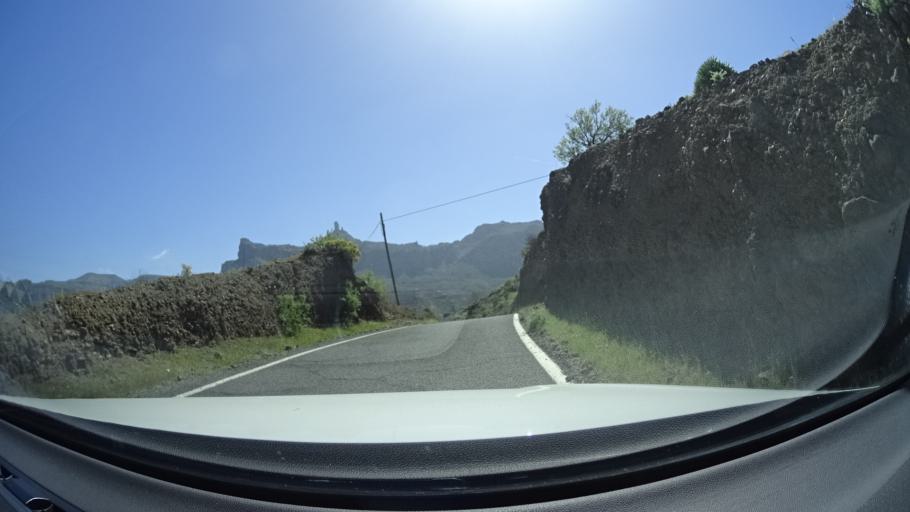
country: ES
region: Canary Islands
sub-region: Provincia de Las Palmas
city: Tejeda
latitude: 27.9893
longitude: -15.6326
